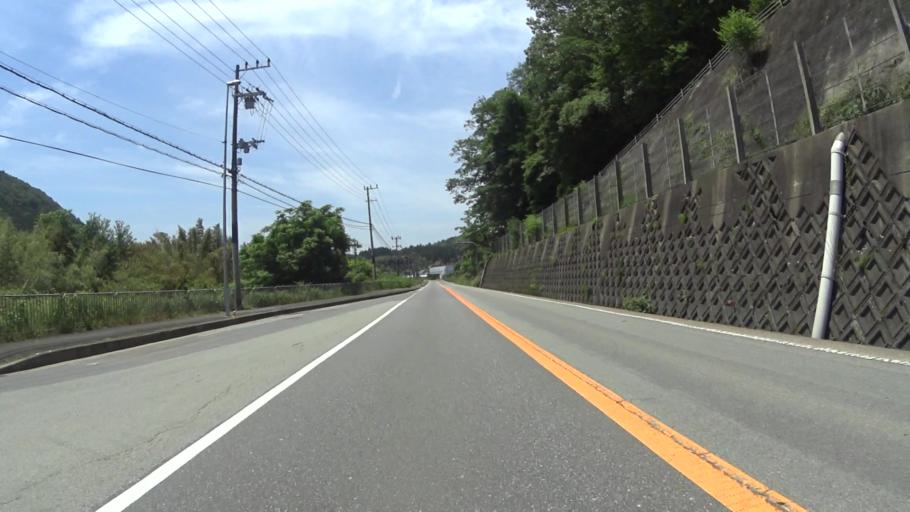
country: JP
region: Kyoto
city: Ayabe
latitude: 35.1793
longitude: 135.3911
